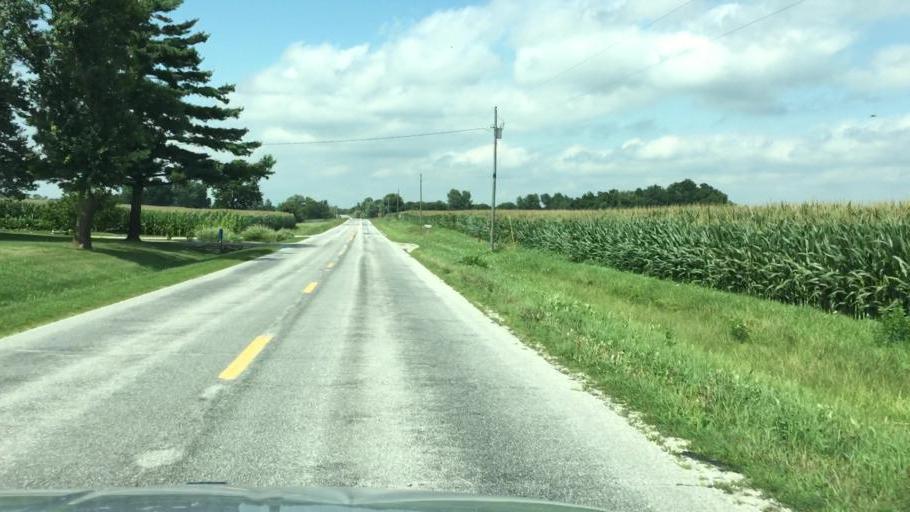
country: US
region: Illinois
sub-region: Hancock County
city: Nauvoo
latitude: 40.5174
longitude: -91.3079
